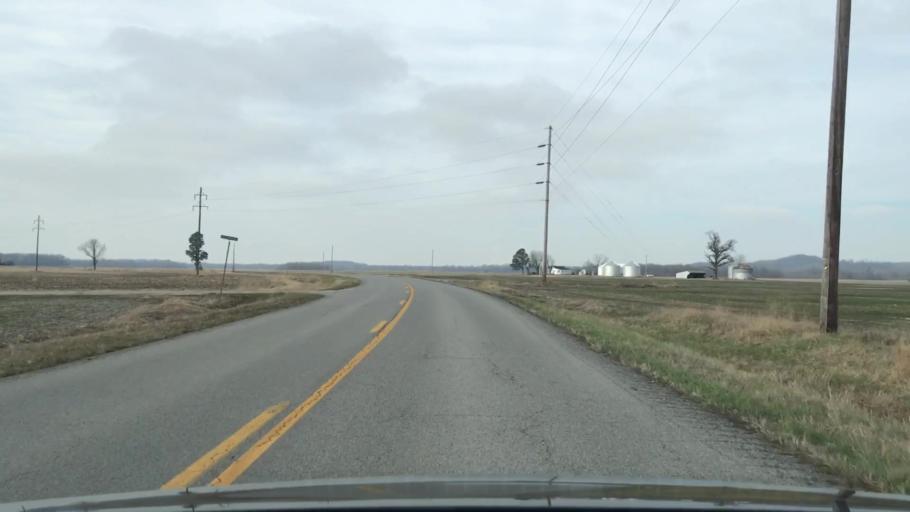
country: US
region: Kentucky
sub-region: McLean County
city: Calhoun
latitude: 37.5333
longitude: -87.3085
